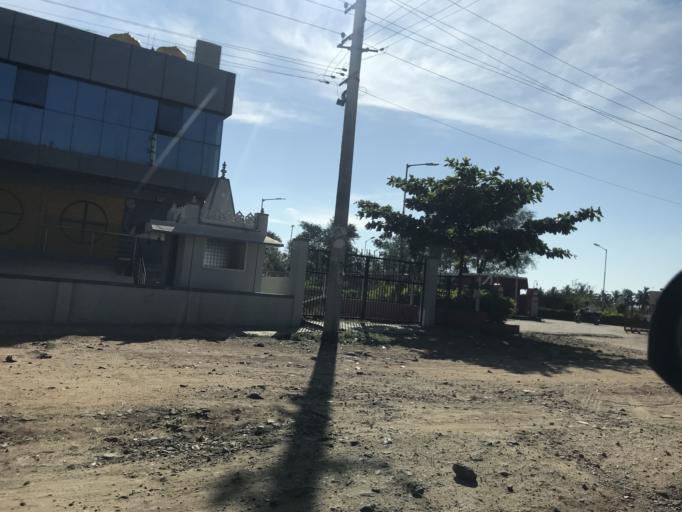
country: IN
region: Karnataka
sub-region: Mysore
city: Mysore
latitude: 12.2073
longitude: 76.5559
